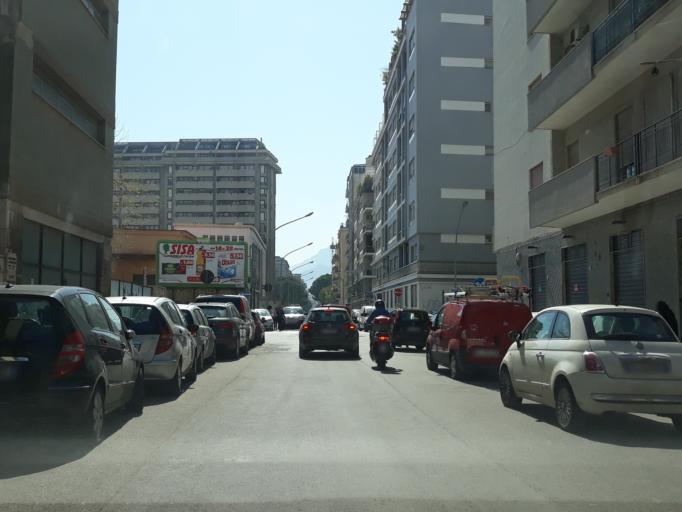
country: IT
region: Sicily
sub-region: Palermo
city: Palermo
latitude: 38.1361
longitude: 13.3525
